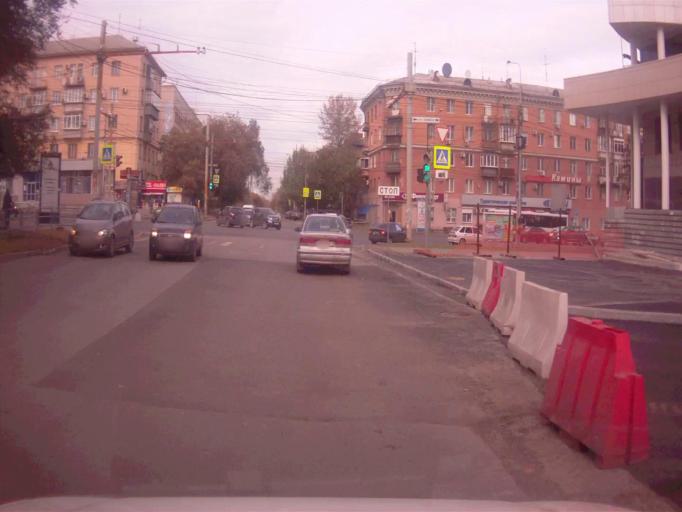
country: RU
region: Chelyabinsk
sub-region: Gorod Chelyabinsk
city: Chelyabinsk
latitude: 55.1603
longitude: 61.4217
